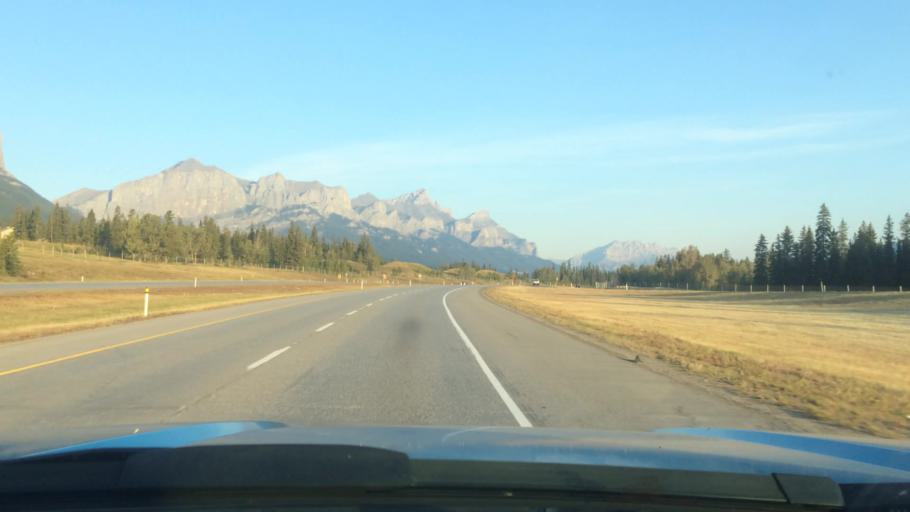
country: CA
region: Alberta
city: Canmore
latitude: 51.0561
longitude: -115.3147
